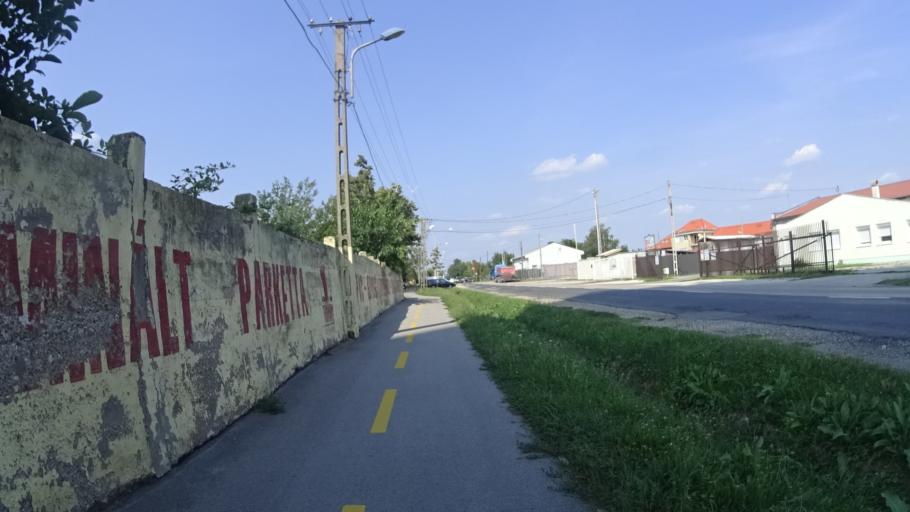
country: HU
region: Zala
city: Nagykanizsa
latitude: 46.4640
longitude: 16.9998
